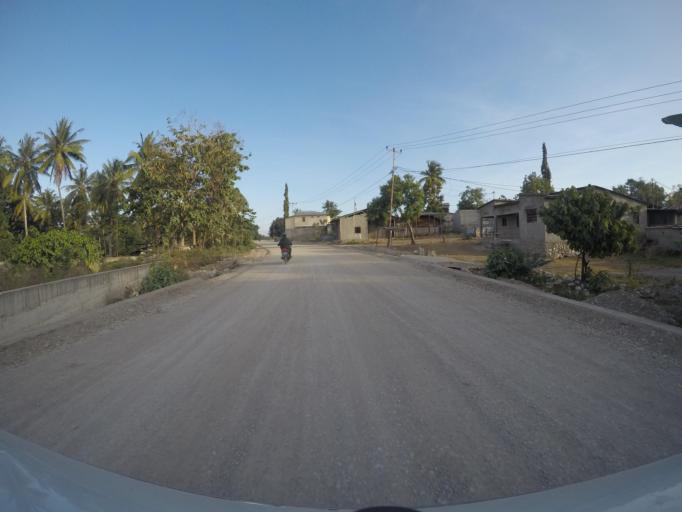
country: TL
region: Viqueque
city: Viqueque
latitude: -8.8468
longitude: 126.5124
